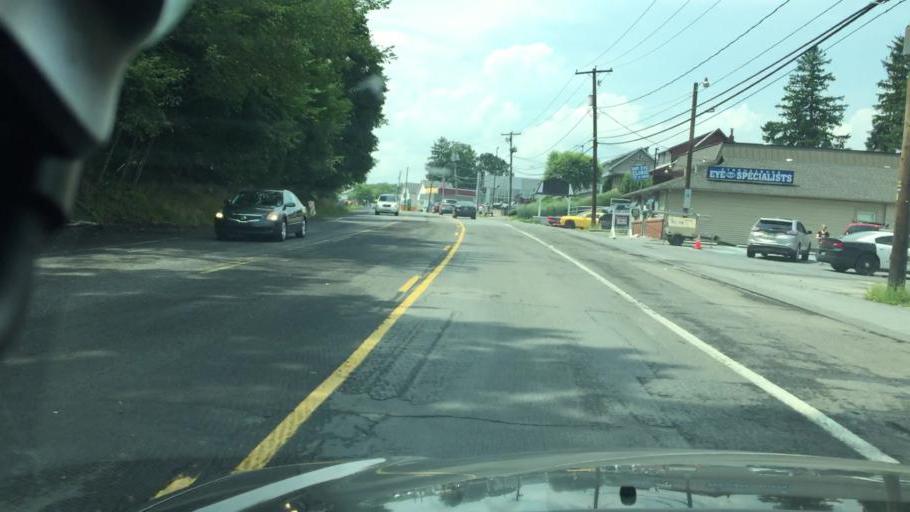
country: US
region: Pennsylvania
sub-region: Monroe County
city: Arlington Heights
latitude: 40.9895
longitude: -75.2118
